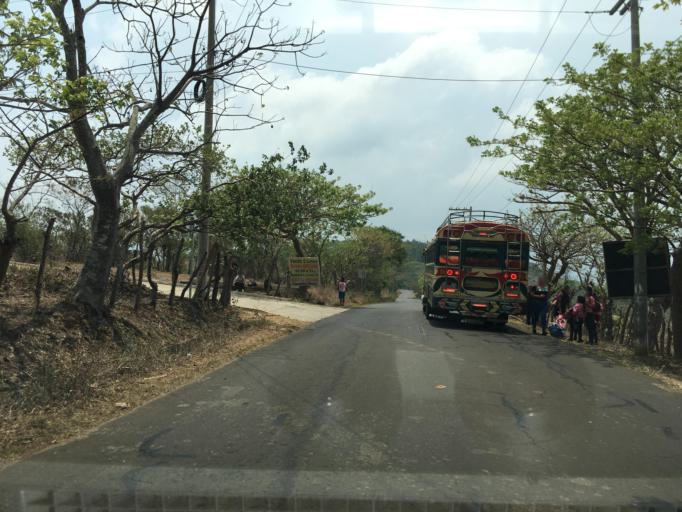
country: GT
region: Santa Rosa
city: Pueblo Nuevo Vinas
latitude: 14.3179
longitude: -90.5563
